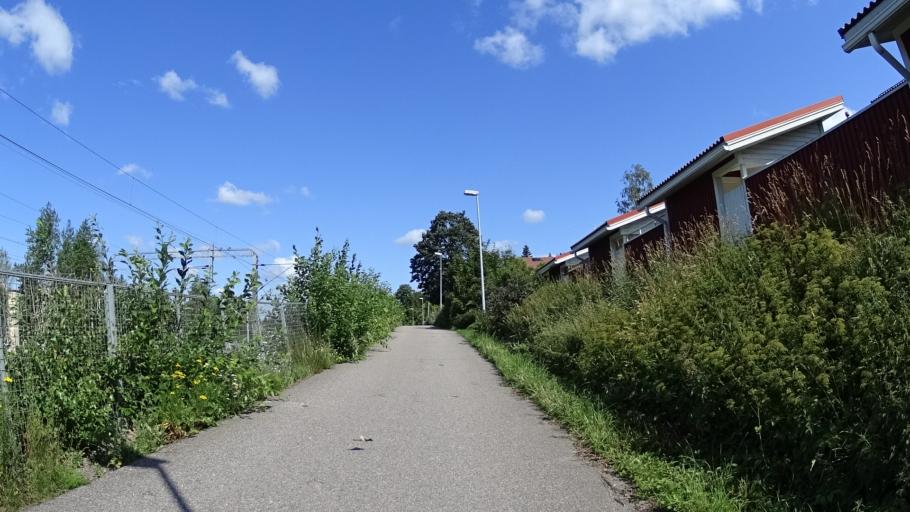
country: FI
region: Uusimaa
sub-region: Helsinki
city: Jaervenpaeae
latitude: 60.4652
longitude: 25.0997
